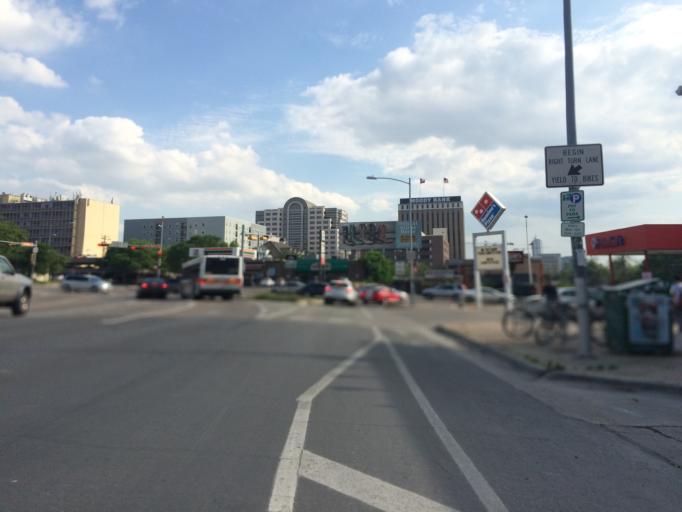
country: US
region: Texas
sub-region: Travis County
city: Austin
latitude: 30.2824
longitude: -97.7422
